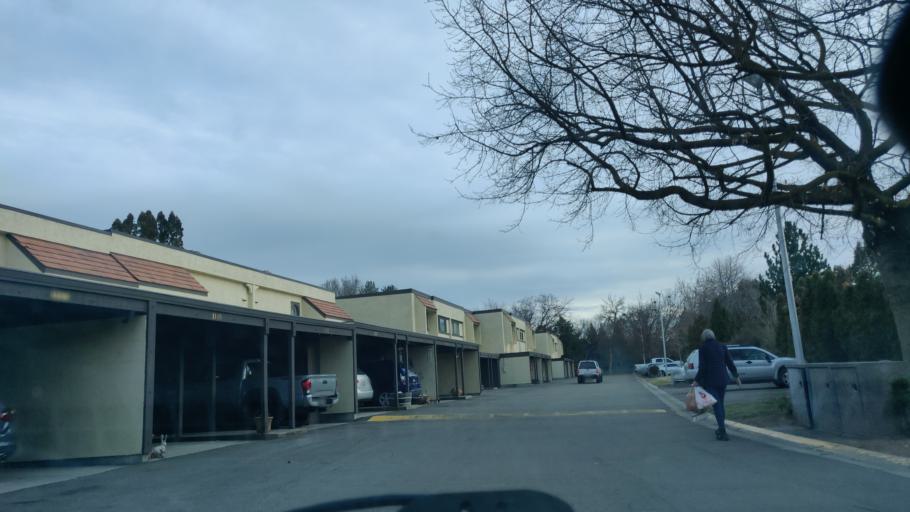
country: US
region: Idaho
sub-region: Ada County
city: Garden City
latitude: 43.6156
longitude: -116.2713
